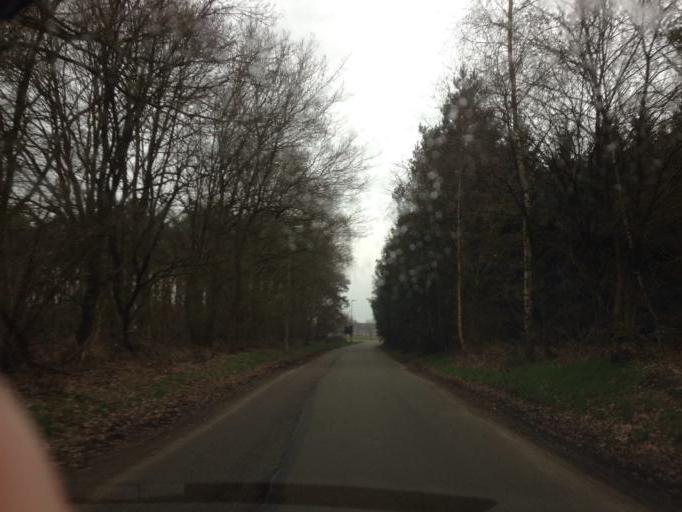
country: BE
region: Flanders
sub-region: Provincie Limburg
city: Opglabbeek
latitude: 51.0849
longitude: 5.5963
